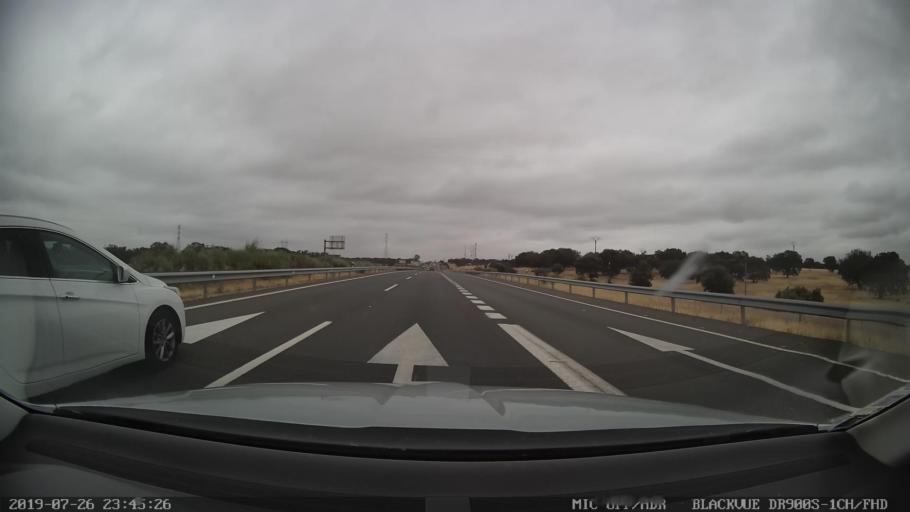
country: ES
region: Extremadura
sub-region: Provincia de Caceres
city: Torrecillas de la Tiesa
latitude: 39.5681
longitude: -5.8337
